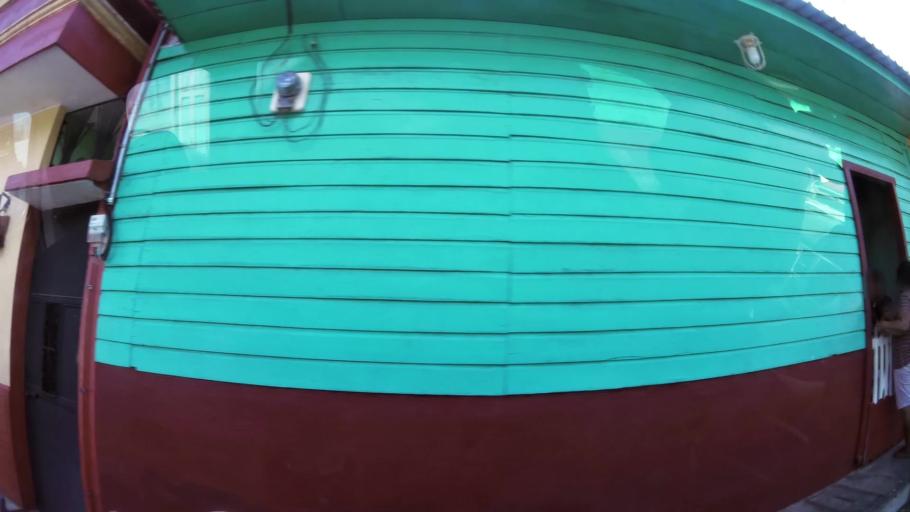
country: GT
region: Suchitepeque
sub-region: Municipio de Cuyotenango
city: Cuyotenango
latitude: 14.5422
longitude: -91.5725
